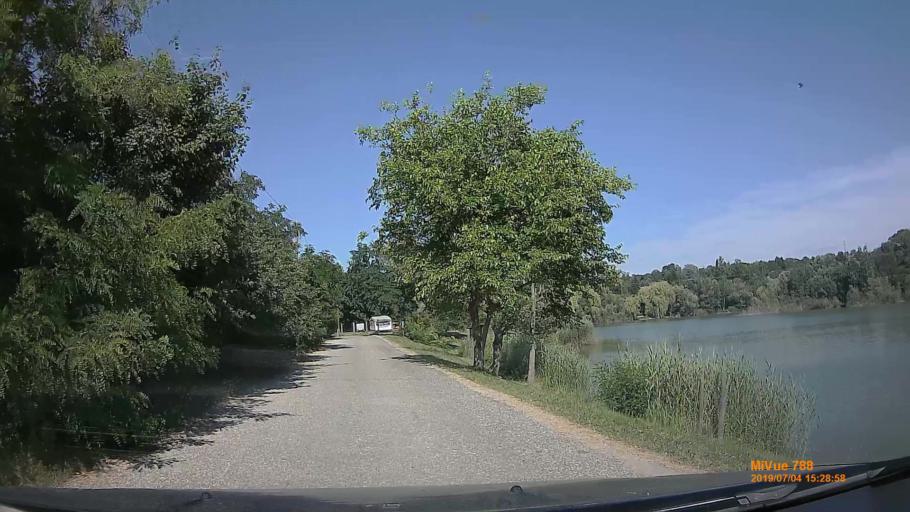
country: HU
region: Komarom-Esztergom
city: Tatabanya
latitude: 47.5380
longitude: 18.3931
